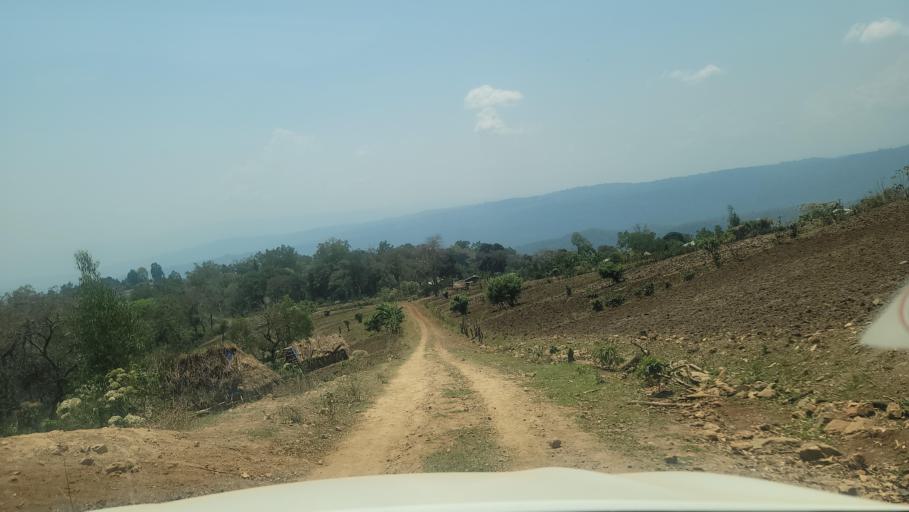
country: ET
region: Southern Nations, Nationalities, and People's Region
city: Bonga
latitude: 7.5367
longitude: 36.1842
